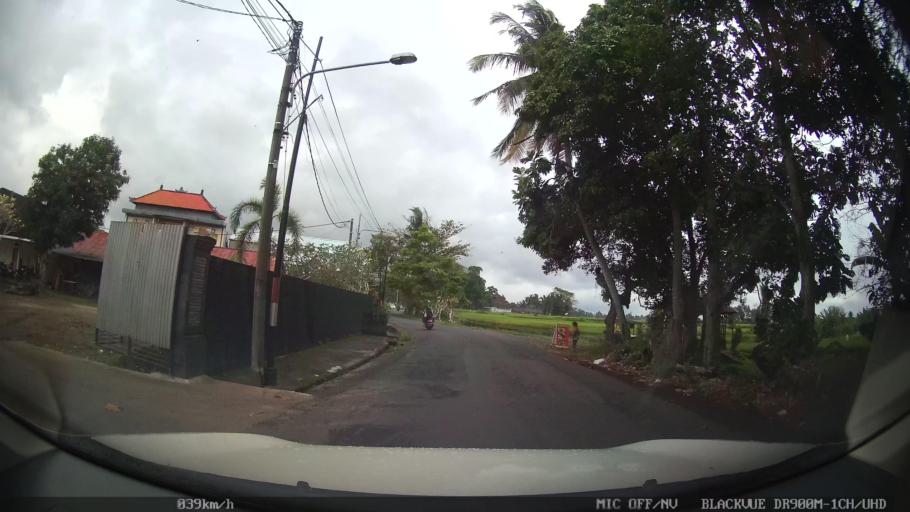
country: ID
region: Bali
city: Banjar Cemenggon
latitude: -8.5520
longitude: 115.1931
